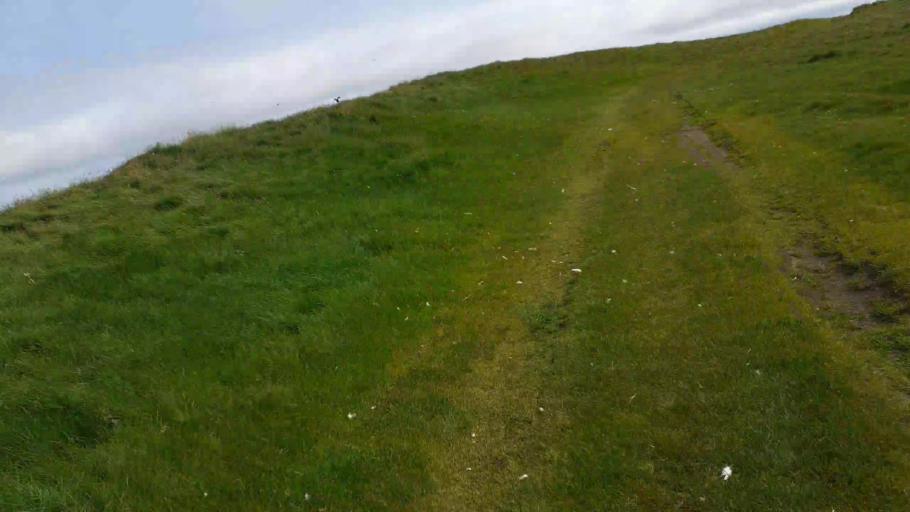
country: IS
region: Northeast
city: Dalvik
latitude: 66.5544
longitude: -18.0005
